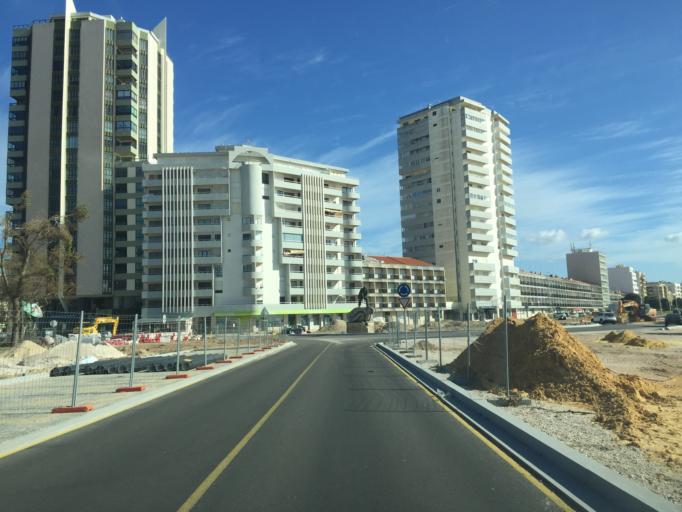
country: PT
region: Coimbra
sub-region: Figueira da Foz
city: Buarcos
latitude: 40.1636
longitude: -8.8741
